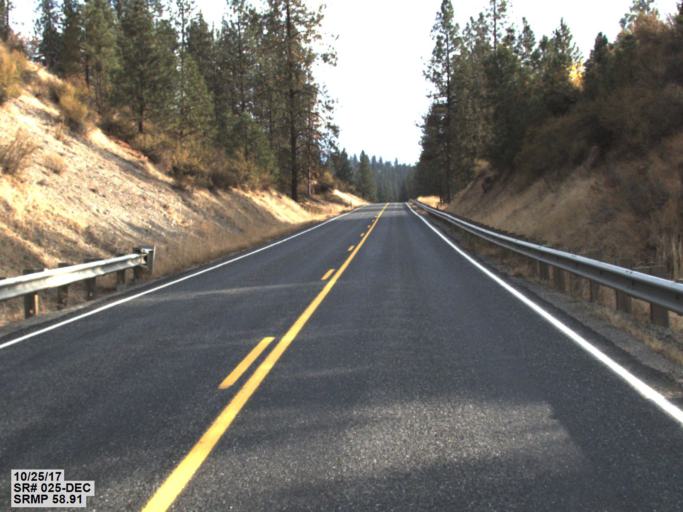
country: US
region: Washington
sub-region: Stevens County
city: Kettle Falls
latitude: 48.3232
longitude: -118.1514
